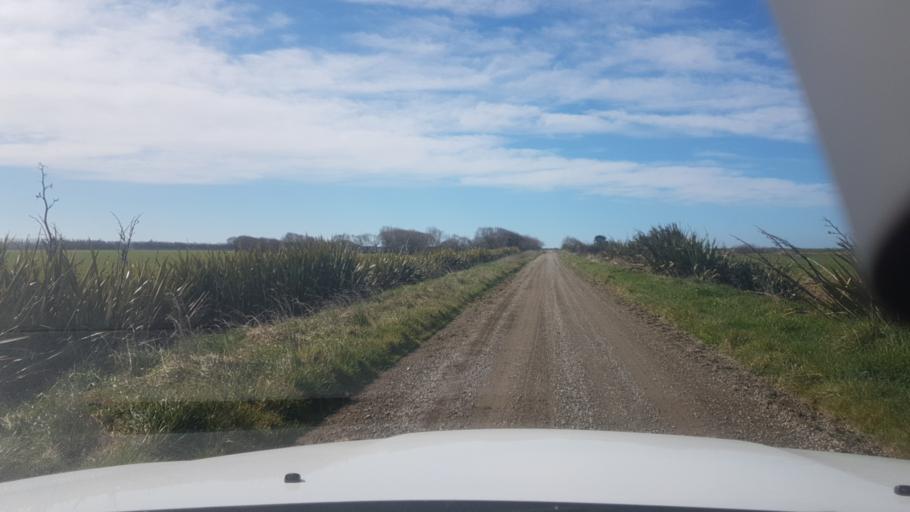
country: NZ
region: Canterbury
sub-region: Timaru District
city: Timaru
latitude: -44.2644
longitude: 171.3643
